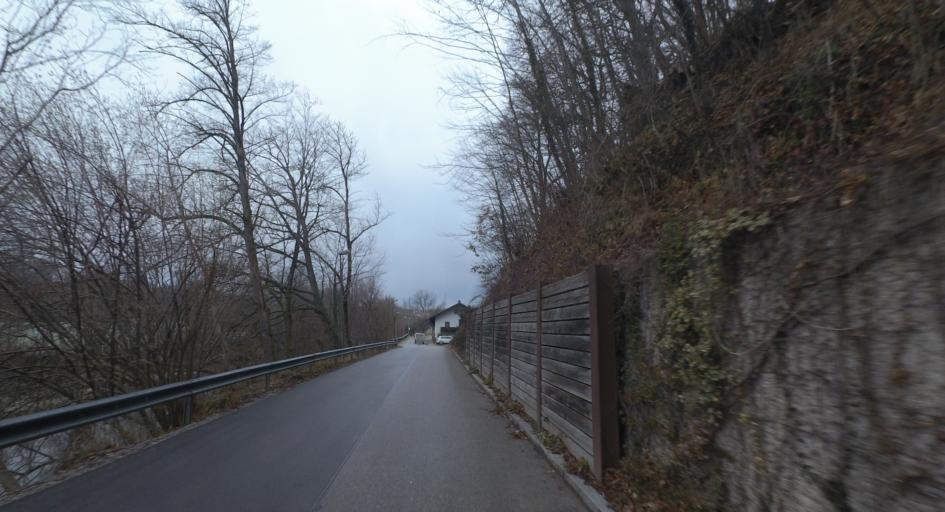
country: DE
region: Bavaria
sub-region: Upper Bavaria
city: Traunreut
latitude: 47.9379
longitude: 12.6015
